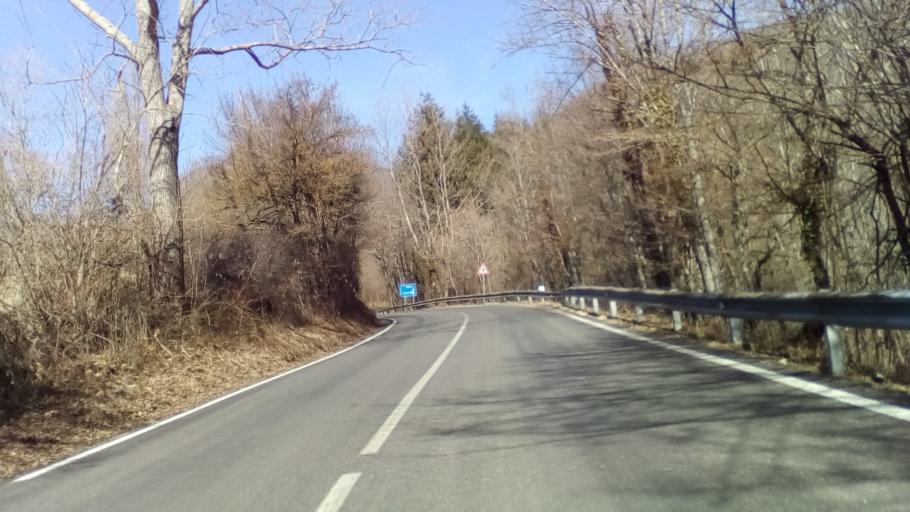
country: IT
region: Emilia-Romagna
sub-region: Provincia di Modena
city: Pievepelago
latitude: 44.2141
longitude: 10.6149
